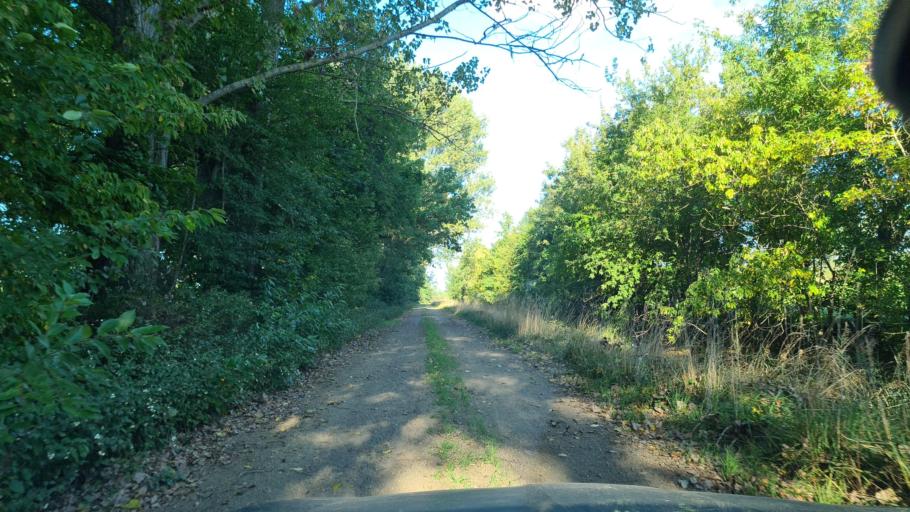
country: DE
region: Brandenburg
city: Bad Liebenwerda
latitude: 51.5267
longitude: 13.3533
